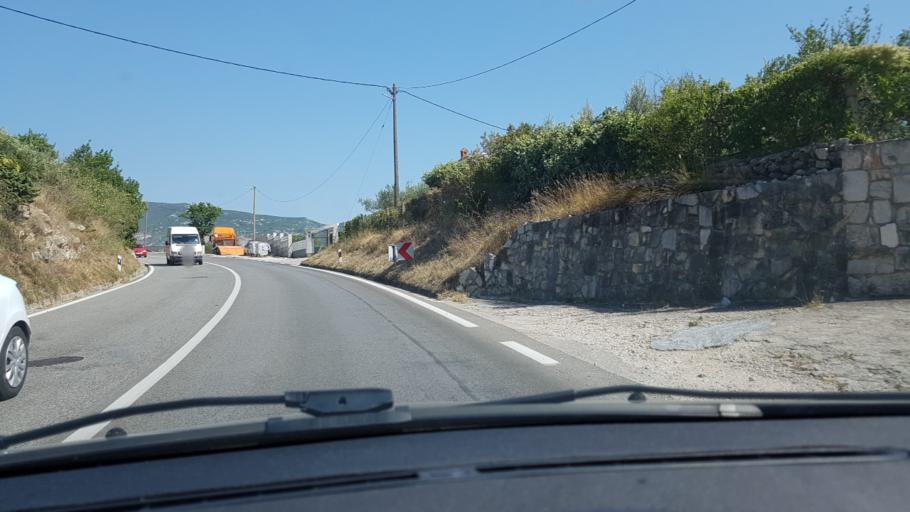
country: HR
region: Splitsko-Dalmatinska
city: Klis
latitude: 43.5565
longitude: 16.5031
